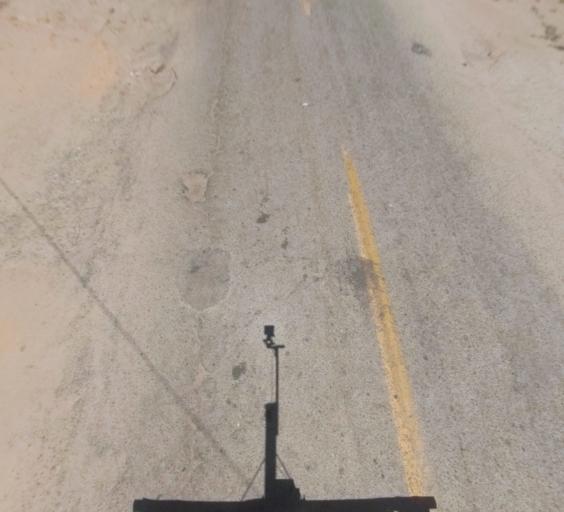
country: US
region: California
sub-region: Madera County
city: Parksdale
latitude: 36.9444
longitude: -120.0229
